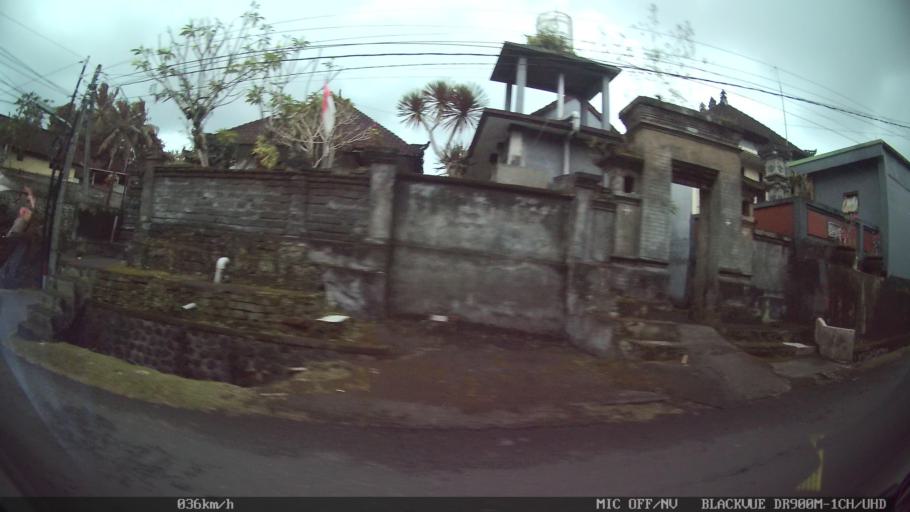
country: ID
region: Bali
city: Banjar Sempidi
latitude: -8.5220
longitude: 115.1907
